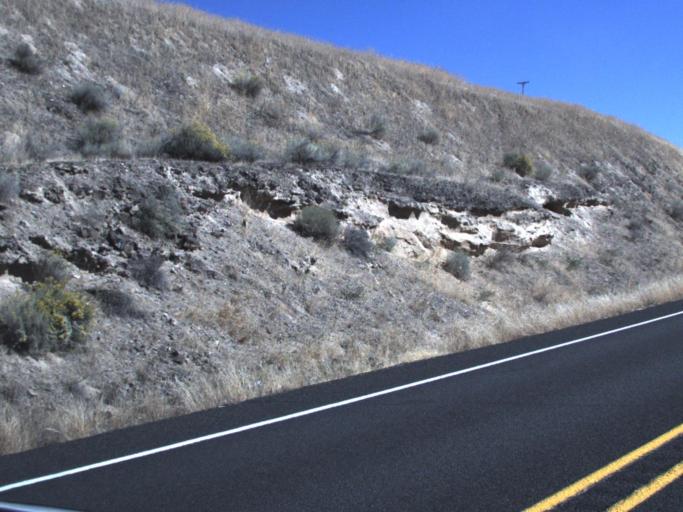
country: US
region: Washington
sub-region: Walla Walla County
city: Garrett
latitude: 46.2883
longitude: -118.4967
